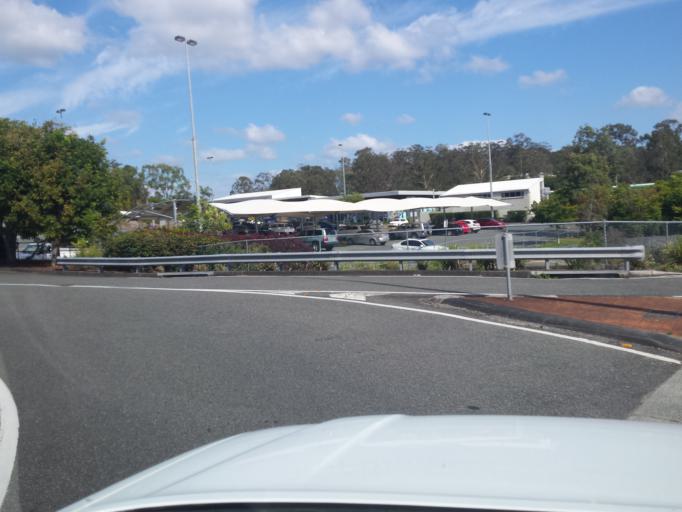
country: AU
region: Queensland
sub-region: Brisbane
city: Bridegman Downs
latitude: -27.3590
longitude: 152.9704
